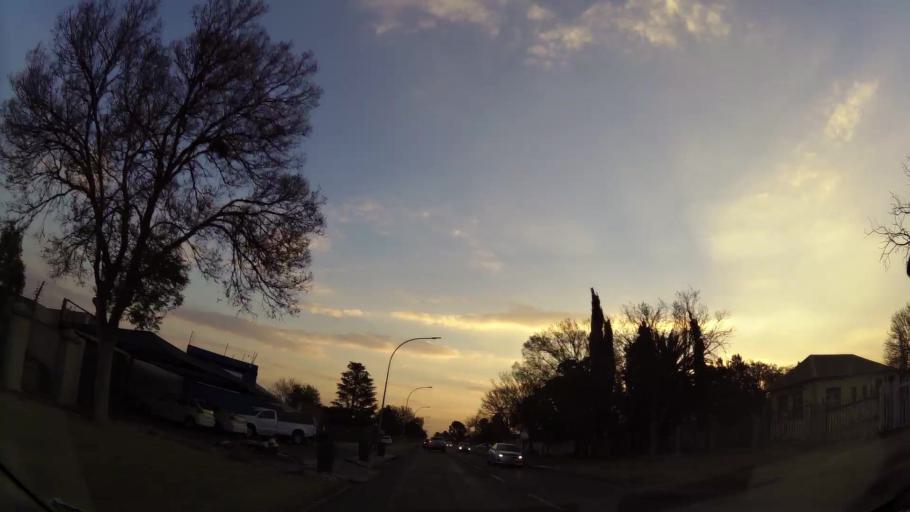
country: ZA
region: Gauteng
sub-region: Ekurhuleni Metropolitan Municipality
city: Benoni
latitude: -26.1751
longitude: 28.3265
